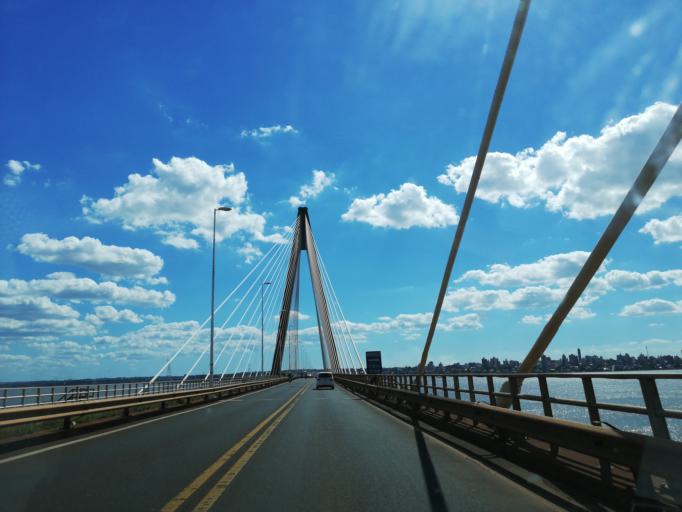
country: AR
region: Misiones
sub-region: Departamento de Capital
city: Posadas
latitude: -27.3691
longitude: -55.8617
